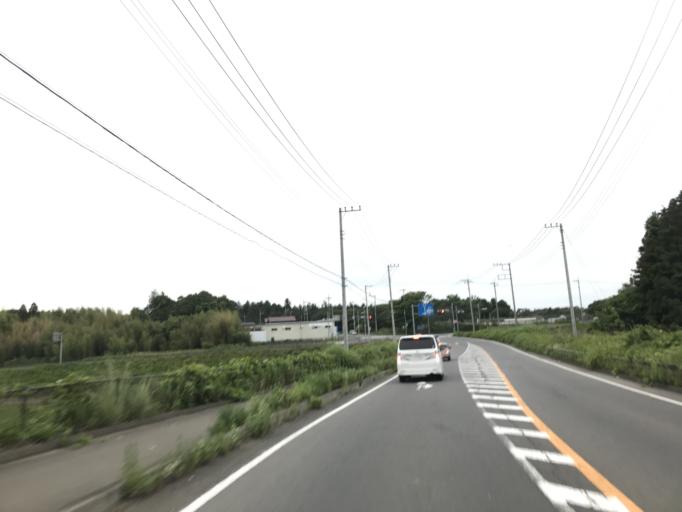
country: JP
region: Ibaraki
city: Ishioka
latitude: 36.2346
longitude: 140.3143
